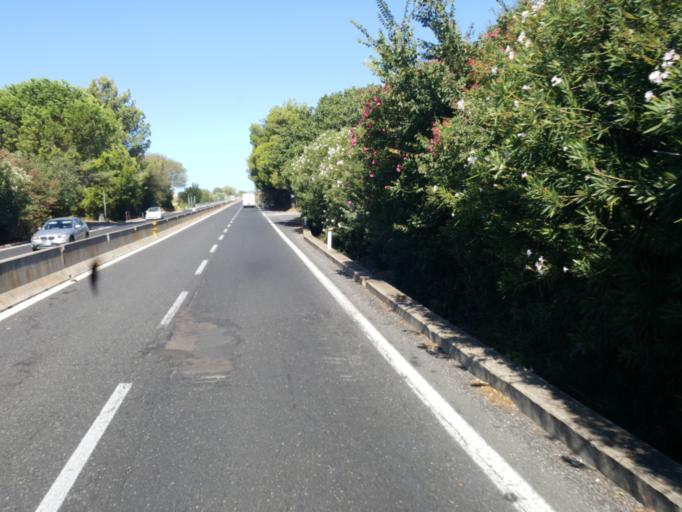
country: IT
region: Latium
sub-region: Provincia di Viterbo
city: Pescia Romana
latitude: 42.4053
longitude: 11.4893
